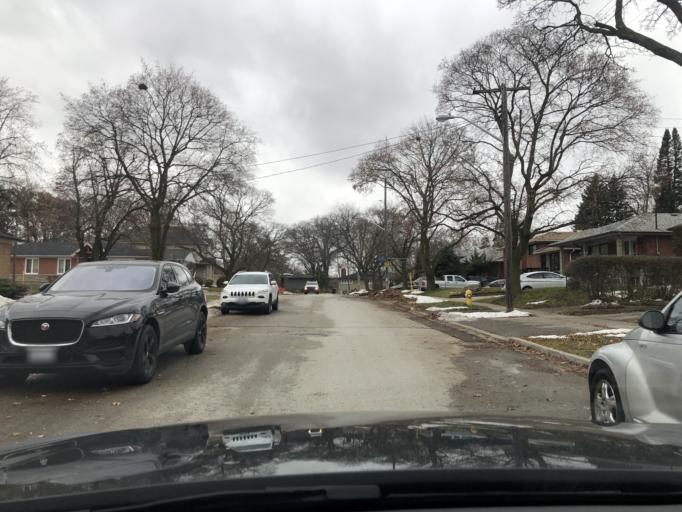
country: CA
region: Ontario
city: Etobicoke
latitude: 43.6935
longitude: -79.5220
